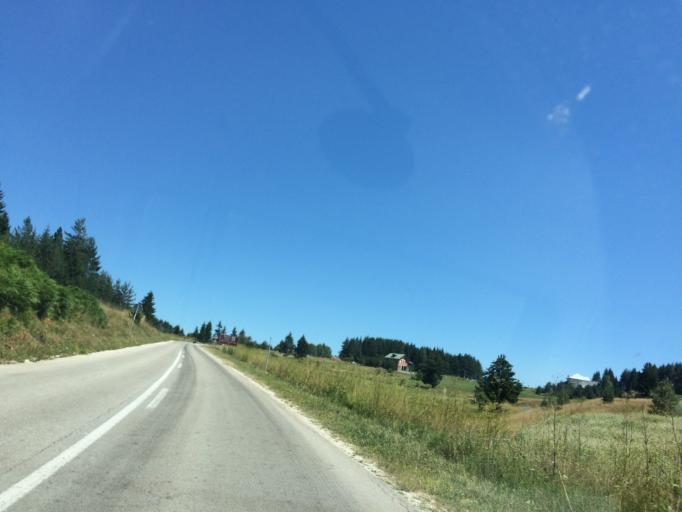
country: RS
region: Central Serbia
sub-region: Zlatiborski Okrug
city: Prijepolje
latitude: 43.3442
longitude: 19.5130
